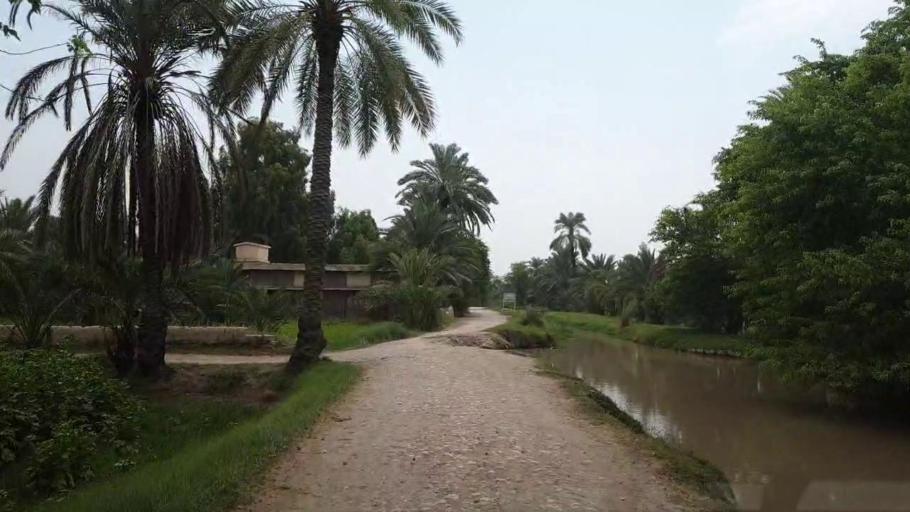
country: PK
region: Sindh
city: Pir jo Goth
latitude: 27.4891
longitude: 68.5948
